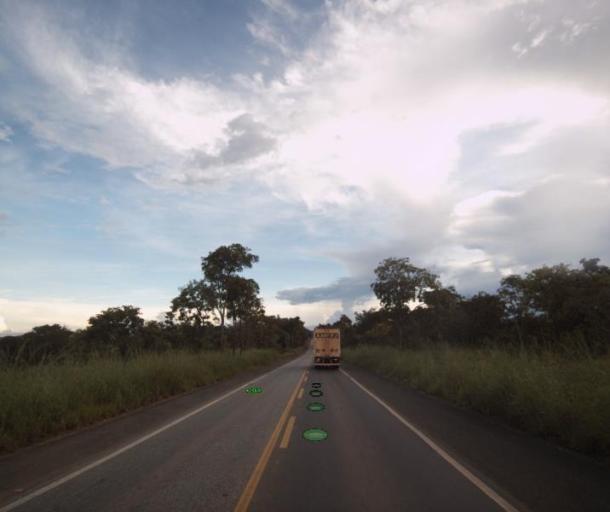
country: BR
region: Goias
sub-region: Uruacu
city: Uruacu
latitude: -14.1243
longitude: -49.1089
